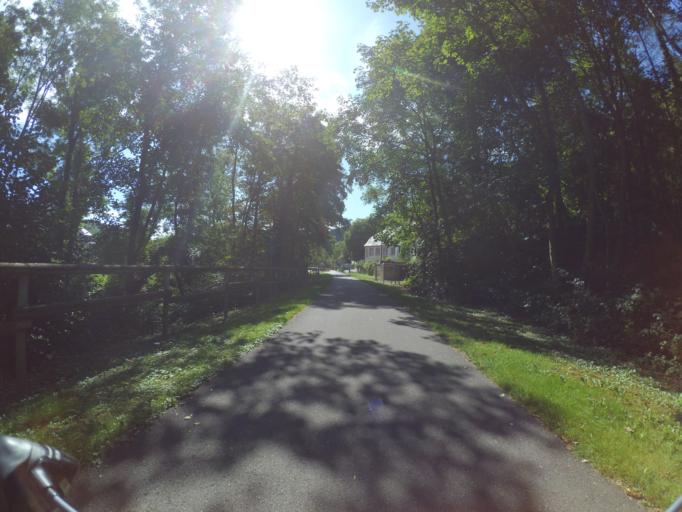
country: DE
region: Rheinland-Pfalz
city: Kasel
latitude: 49.7633
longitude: 6.7261
